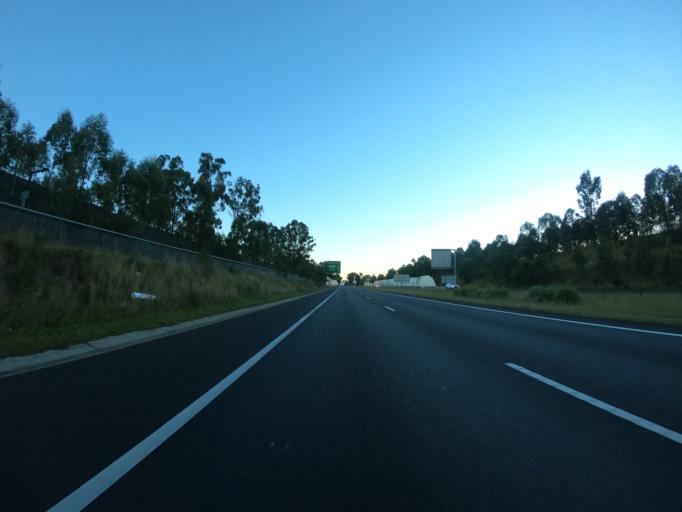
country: AU
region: New South Wales
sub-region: Blacktown
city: Glendenning
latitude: -33.7453
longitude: 150.8464
